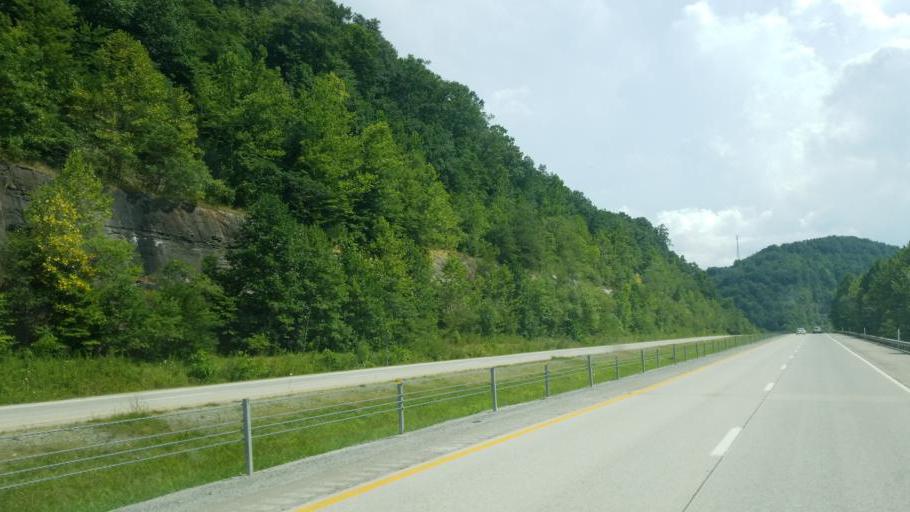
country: US
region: West Virginia
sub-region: Boone County
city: Madison
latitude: 38.1709
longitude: -81.8502
